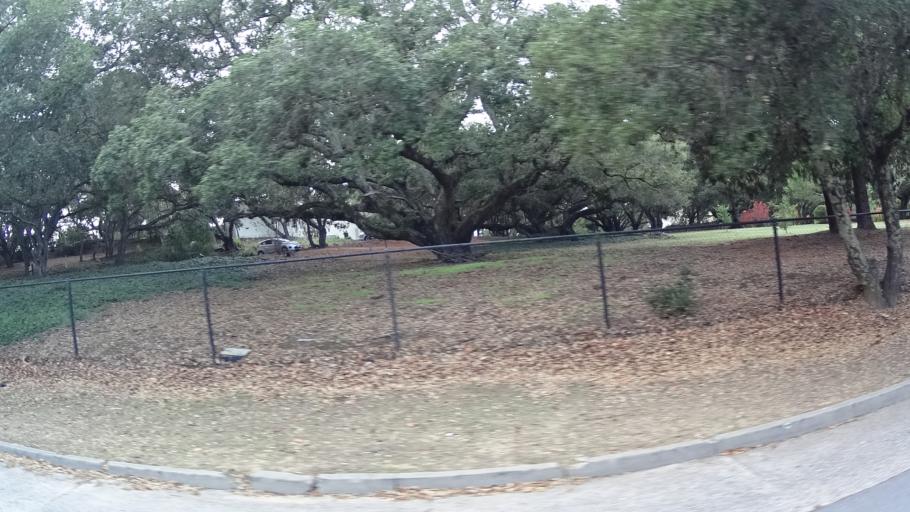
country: US
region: California
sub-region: San Mateo County
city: Hillsborough
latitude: 37.5828
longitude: -122.3812
